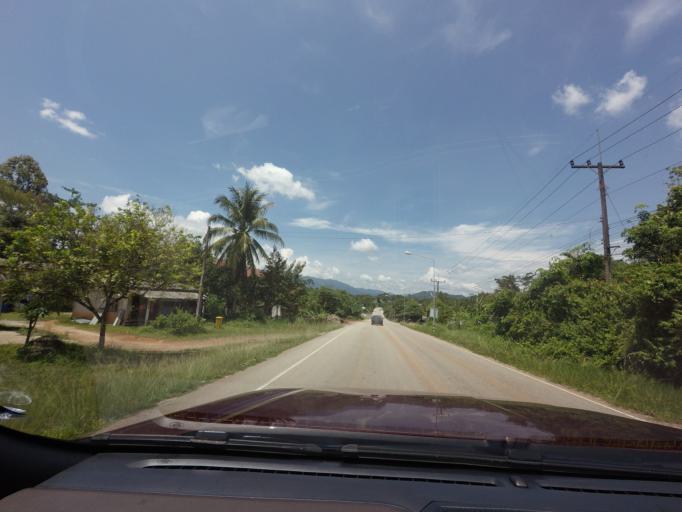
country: TH
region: Narathiwat
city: Chanae
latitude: 6.1814
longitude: 101.6978
